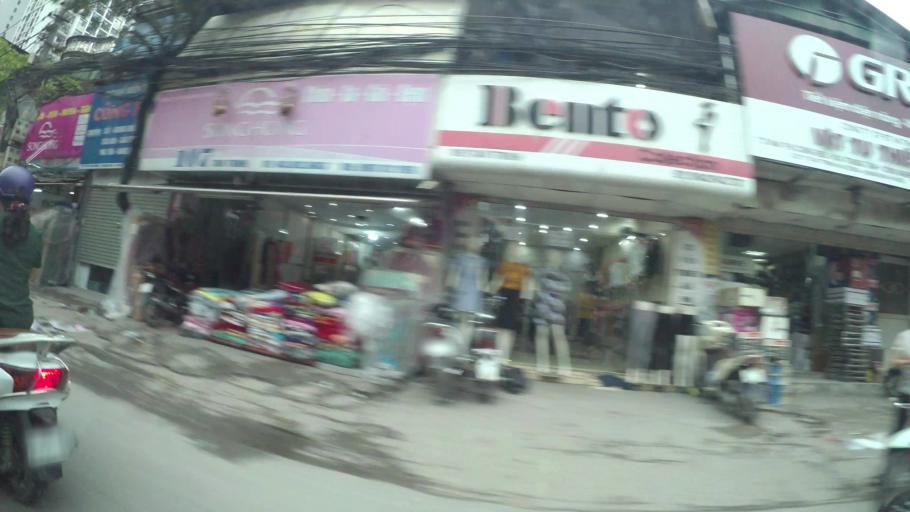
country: VN
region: Ha Noi
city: Hai BaTrung
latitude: 20.9935
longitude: 105.8629
